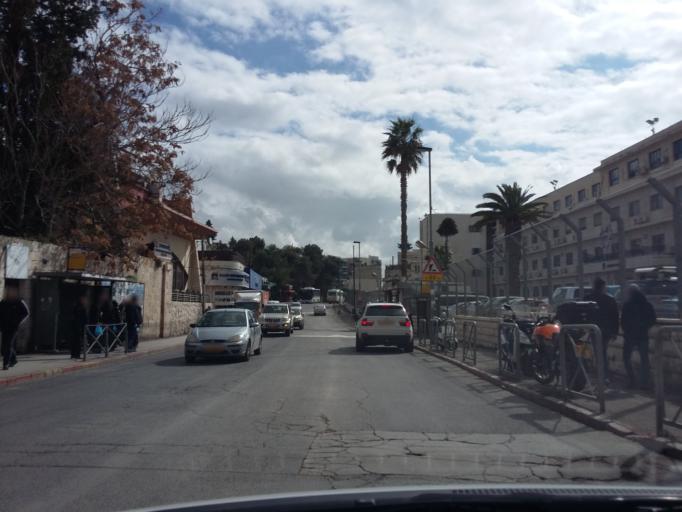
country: PS
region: West Bank
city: East Jerusalem
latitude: 31.7875
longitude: 35.2299
